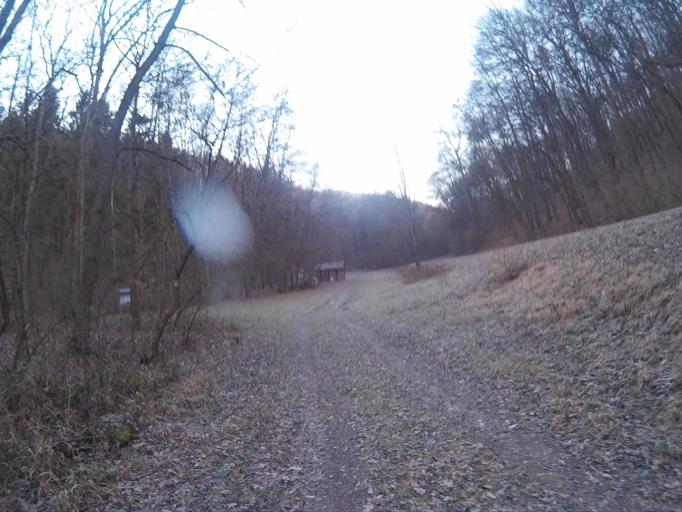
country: HU
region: Borsod-Abauj-Zemplen
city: Putnok
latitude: 48.3316
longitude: 20.4346
